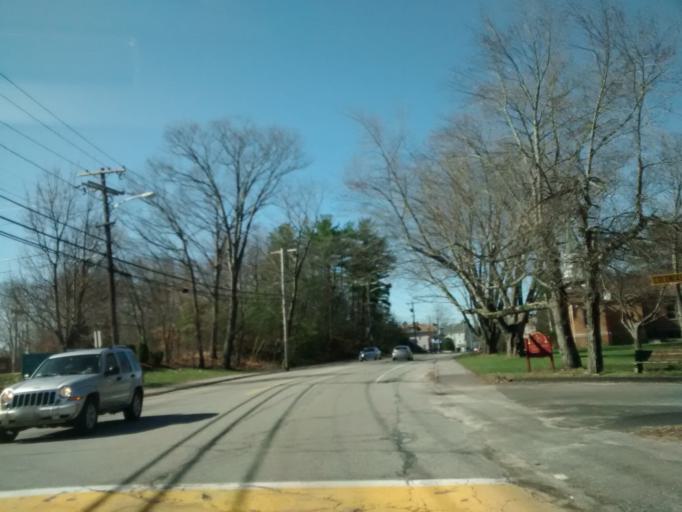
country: US
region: Massachusetts
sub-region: Worcester County
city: Whitinsville
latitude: 42.1156
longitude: -71.6538
